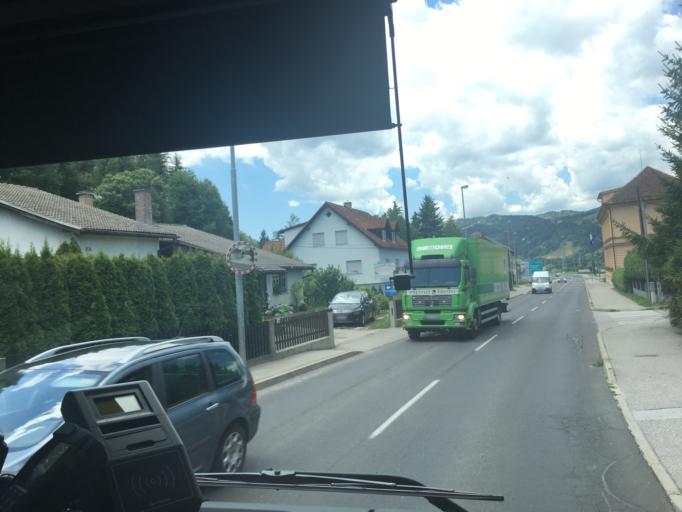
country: SI
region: Maribor
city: Limbus
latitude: 46.5555
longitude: 15.5801
